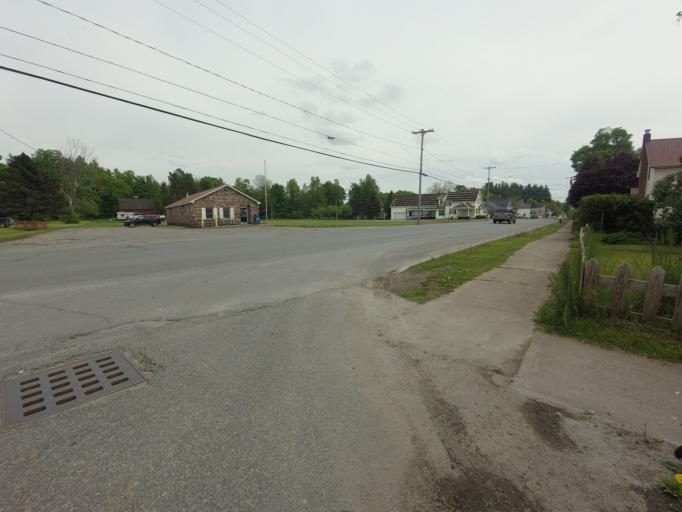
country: US
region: New York
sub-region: St. Lawrence County
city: Gouverneur
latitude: 44.3269
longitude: -75.2495
